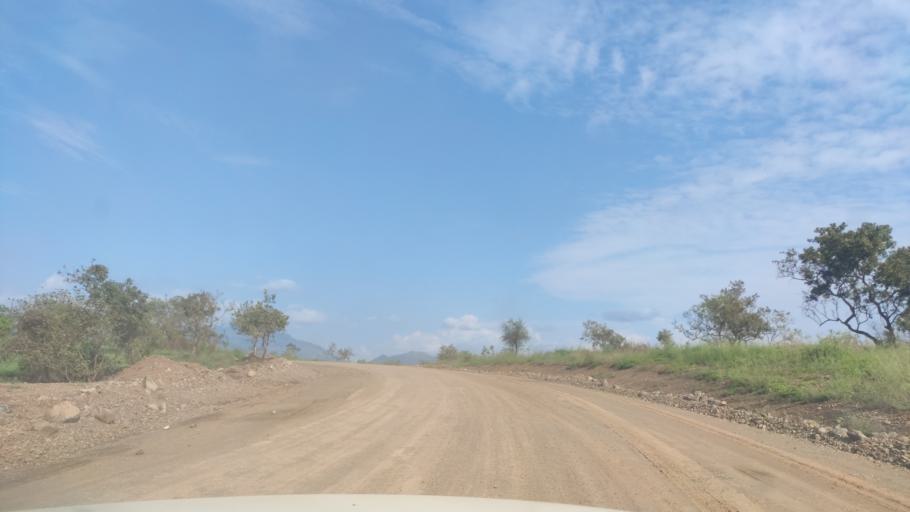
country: ET
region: Southern Nations, Nationalities, and People's Region
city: Felege Neway
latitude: 6.4245
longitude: 37.2207
